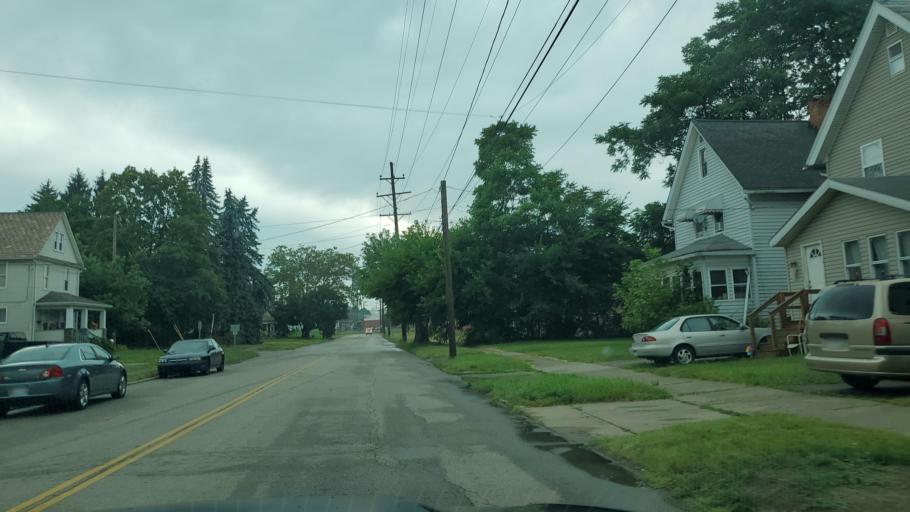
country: US
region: Ohio
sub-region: Trumbull County
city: Warren
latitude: 41.2455
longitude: -80.8095
